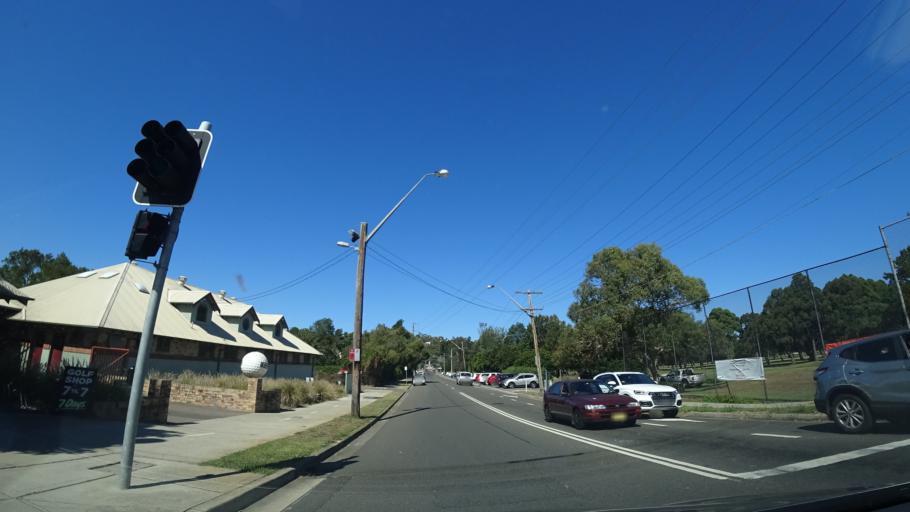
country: AU
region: New South Wales
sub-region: Warringah
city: North Manly
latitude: -33.7764
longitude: 151.2668
